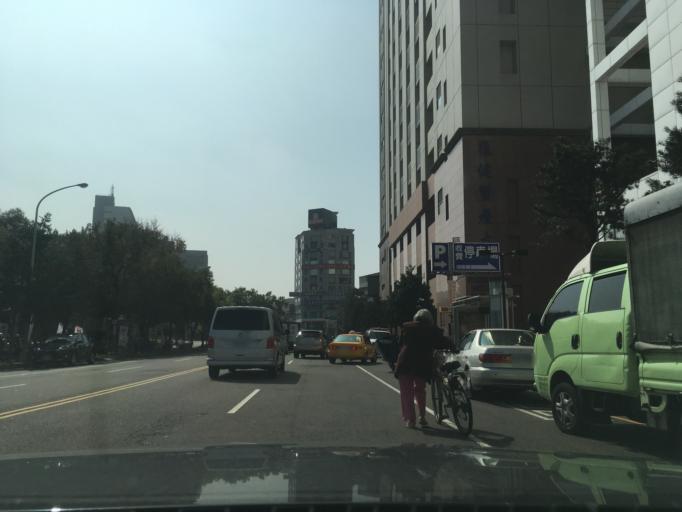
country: TW
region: Taiwan
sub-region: Taichung City
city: Taichung
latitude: 24.1570
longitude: 120.6812
